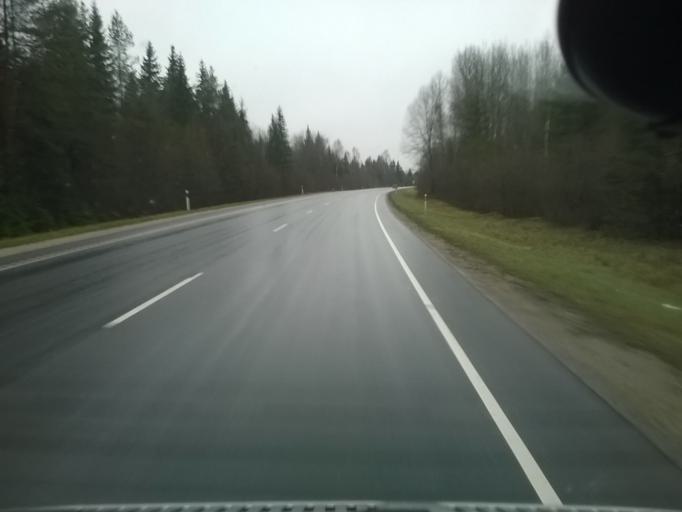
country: EE
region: Harju
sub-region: Nissi vald
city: Turba
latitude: 59.1094
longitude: 24.2561
